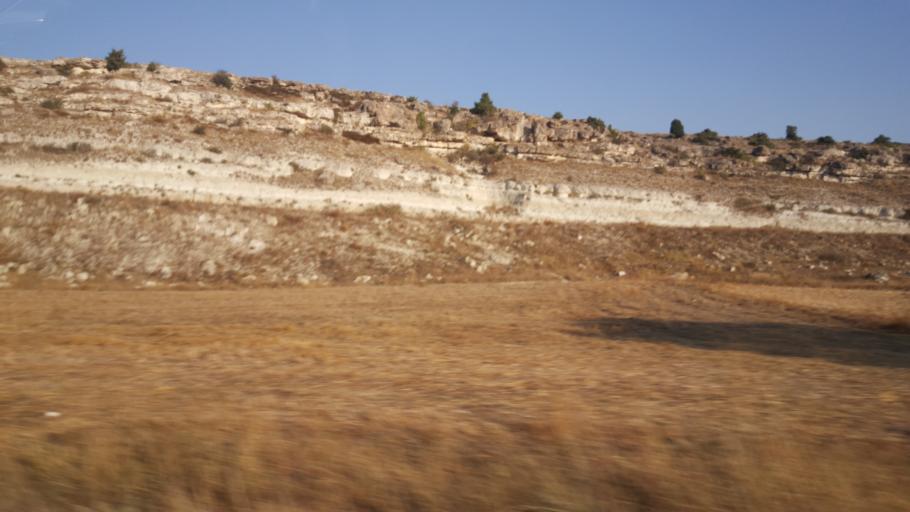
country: TR
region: Eskisehir
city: Seyitgazi
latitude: 39.4197
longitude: 30.6512
